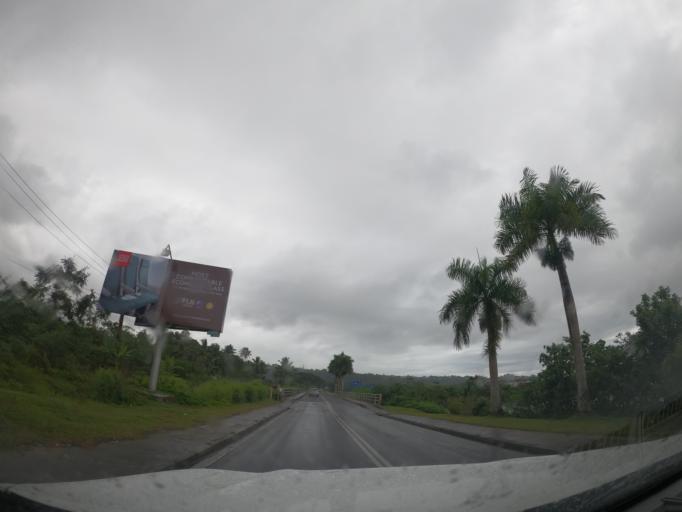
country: FJ
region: Central
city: Suva
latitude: -18.1130
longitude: 178.4233
